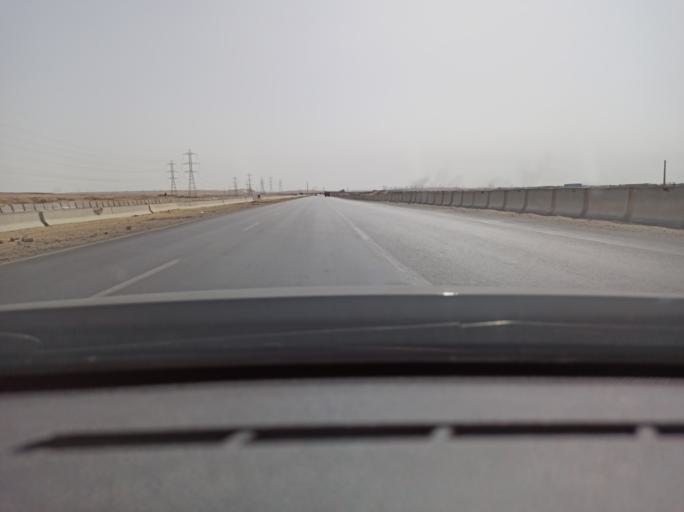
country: EG
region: Muhafazat al Qahirah
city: Halwan
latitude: 29.7712
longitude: 31.3744
